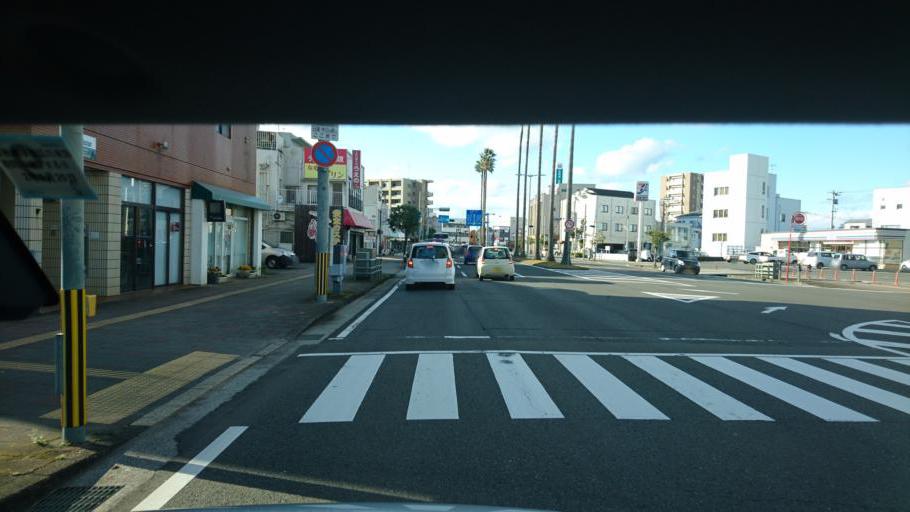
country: JP
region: Miyazaki
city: Miyazaki-shi
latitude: 31.8970
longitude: 131.4195
